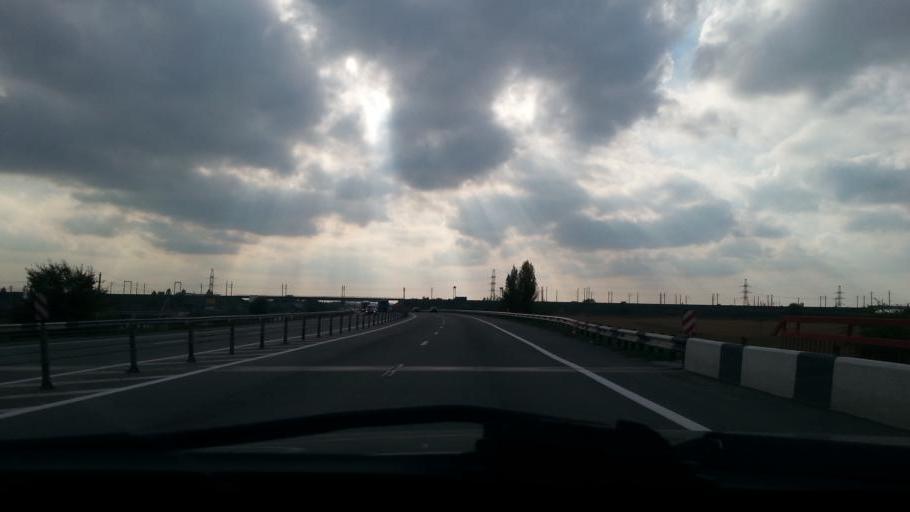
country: RU
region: Rostov
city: Bataysk
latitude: 47.1477
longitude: 39.7046
